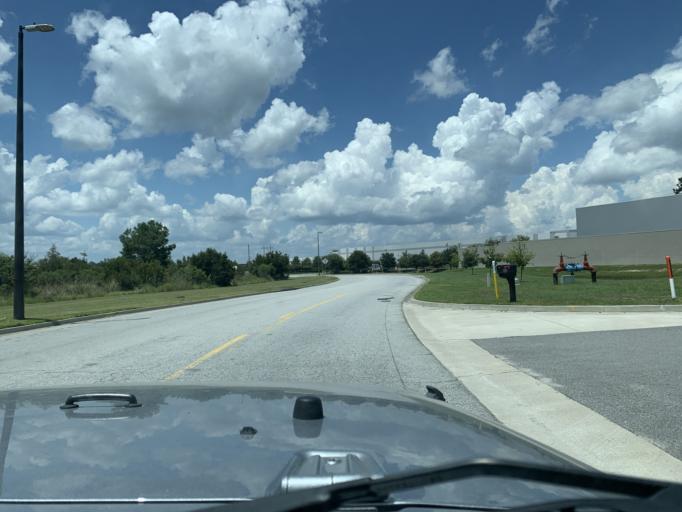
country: US
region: Georgia
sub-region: Chatham County
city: Pooler
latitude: 32.1026
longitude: -81.2698
